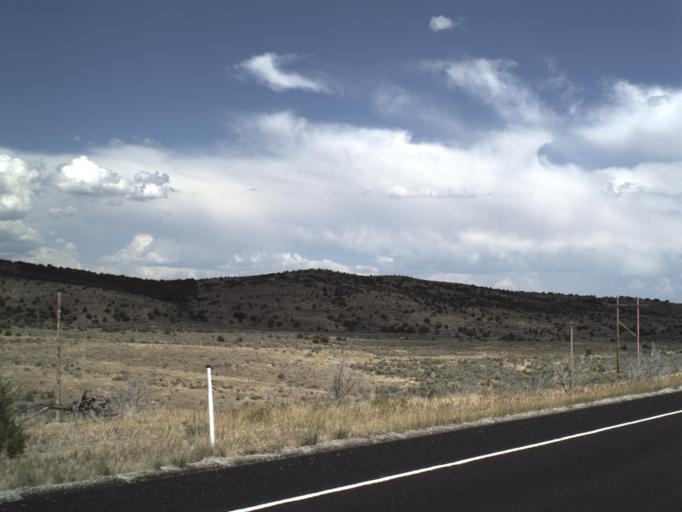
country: US
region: Idaho
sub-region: Minidoka County
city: Rupert
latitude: 41.9797
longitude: -113.1661
